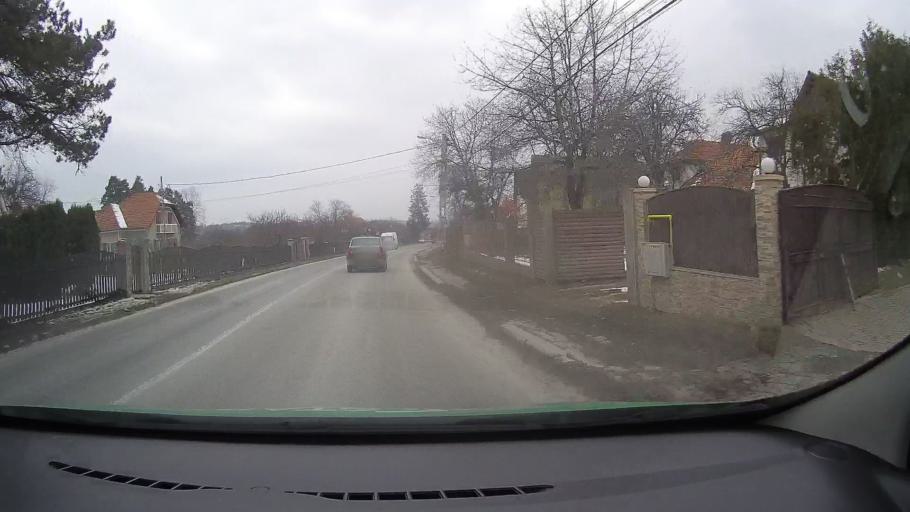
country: RO
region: Brasov
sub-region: Comuna Bran
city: Bran
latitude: 45.5202
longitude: 25.3704
